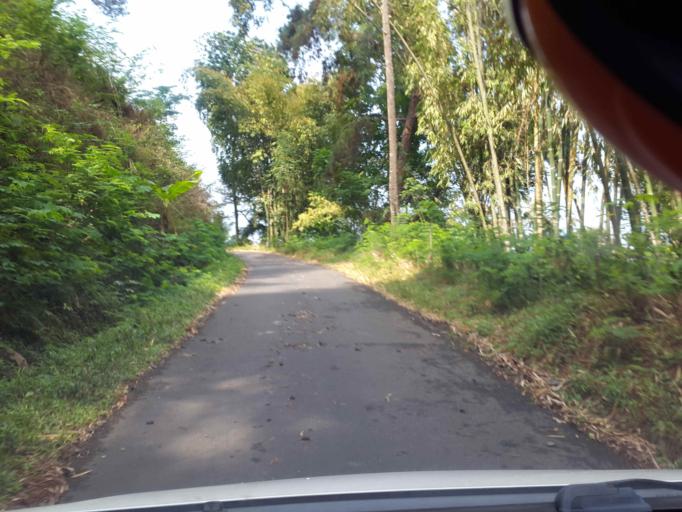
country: ID
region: East Java
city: Ponorogo
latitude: -7.7973
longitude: 111.6439
